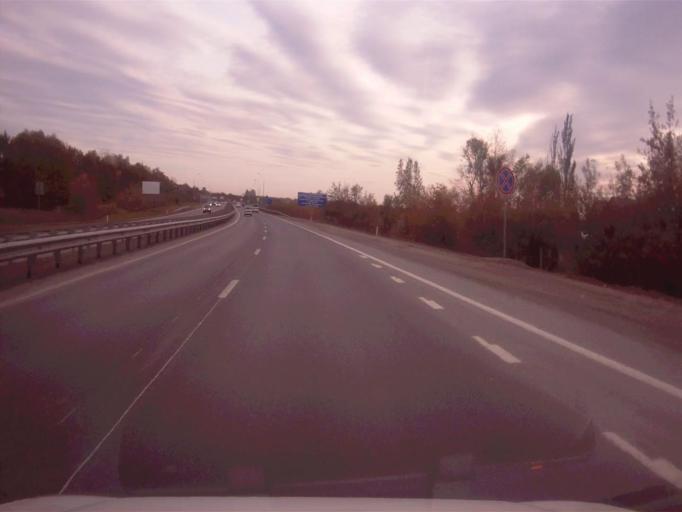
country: RU
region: Chelyabinsk
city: Novosineglazovskiy
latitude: 55.0351
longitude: 61.4422
